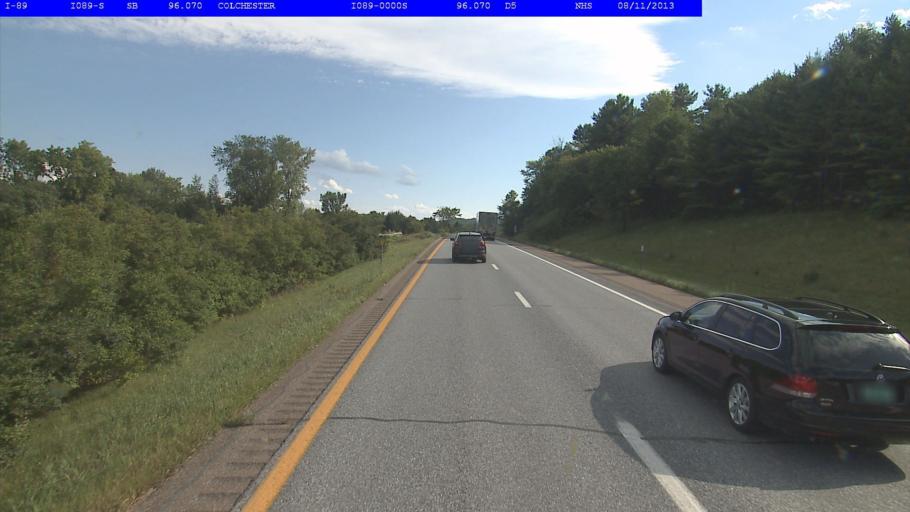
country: US
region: Vermont
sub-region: Chittenden County
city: Colchester
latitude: 44.5648
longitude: -73.1794
